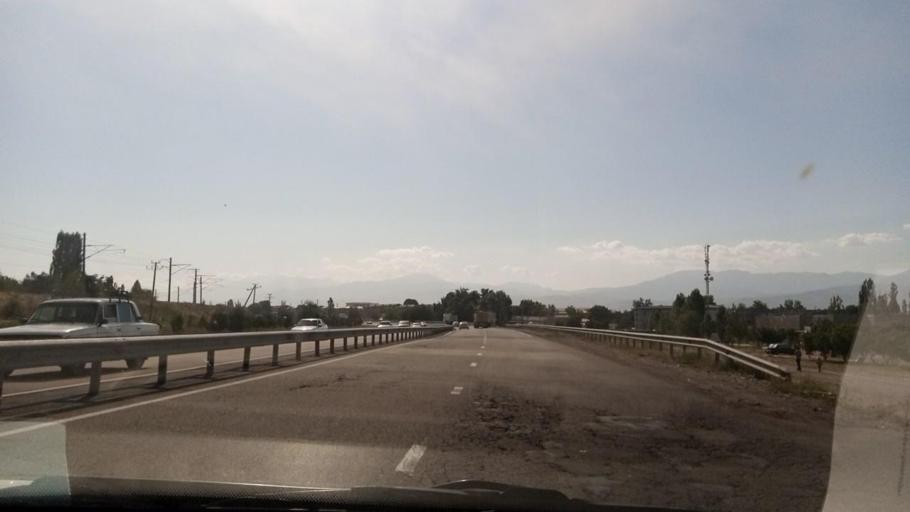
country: UZ
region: Toshkent
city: Ohangaron
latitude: 40.9080
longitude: 69.7940
